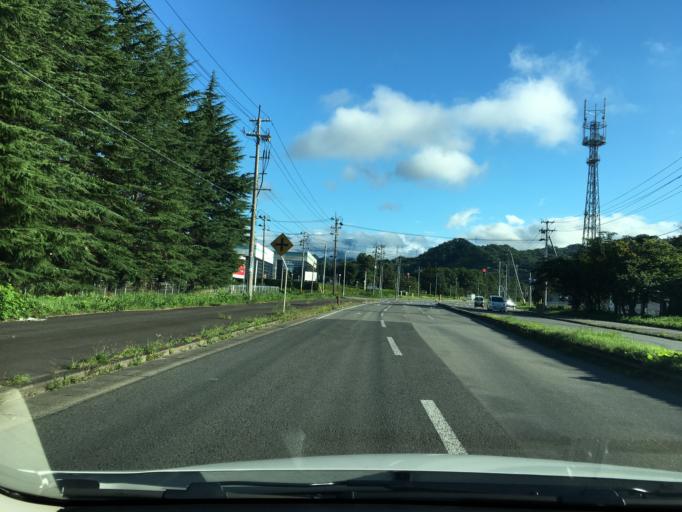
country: JP
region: Yamagata
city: Yonezawa
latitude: 37.9042
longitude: 140.1669
